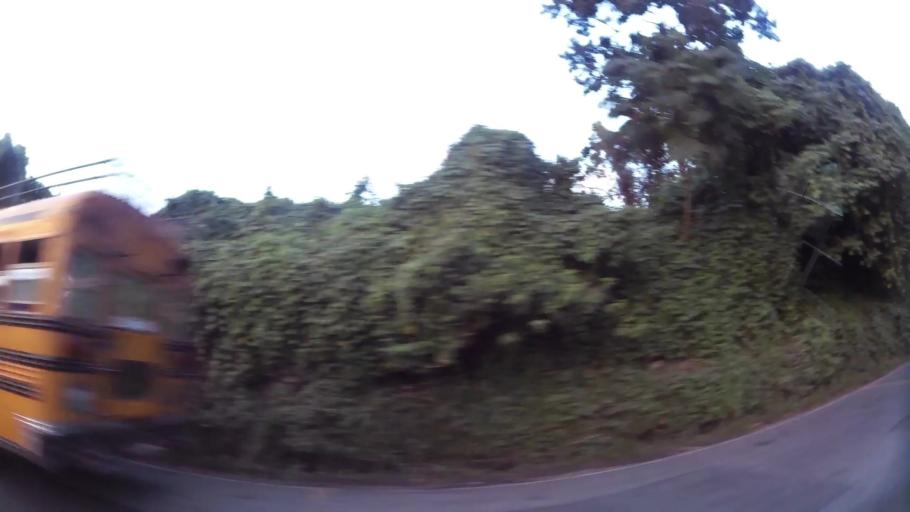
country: GT
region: Retalhuleu
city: Santa Cruz Mulua
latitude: 14.5748
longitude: -91.6320
